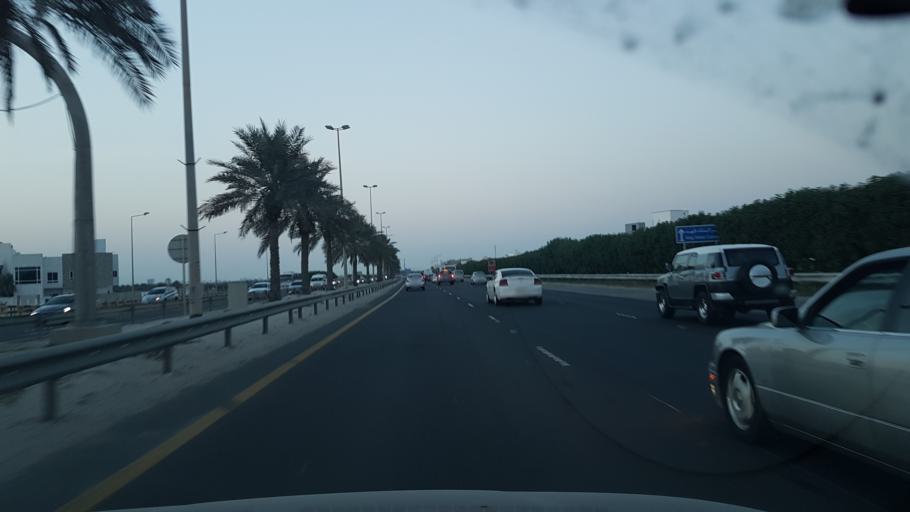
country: BH
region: Central Governorate
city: Madinat Hamad
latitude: 26.1495
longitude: 50.5087
